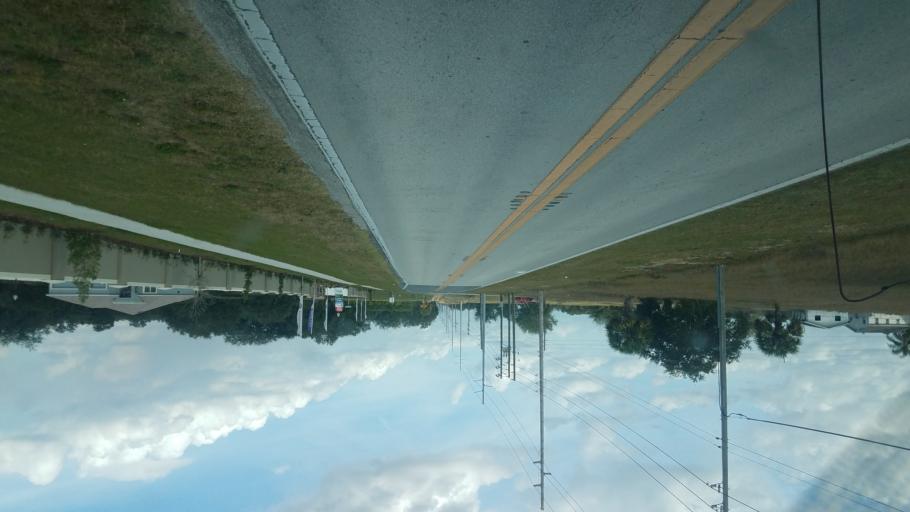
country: US
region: Florida
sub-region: Polk County
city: Davenport
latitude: 28.1527
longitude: -81.5903
